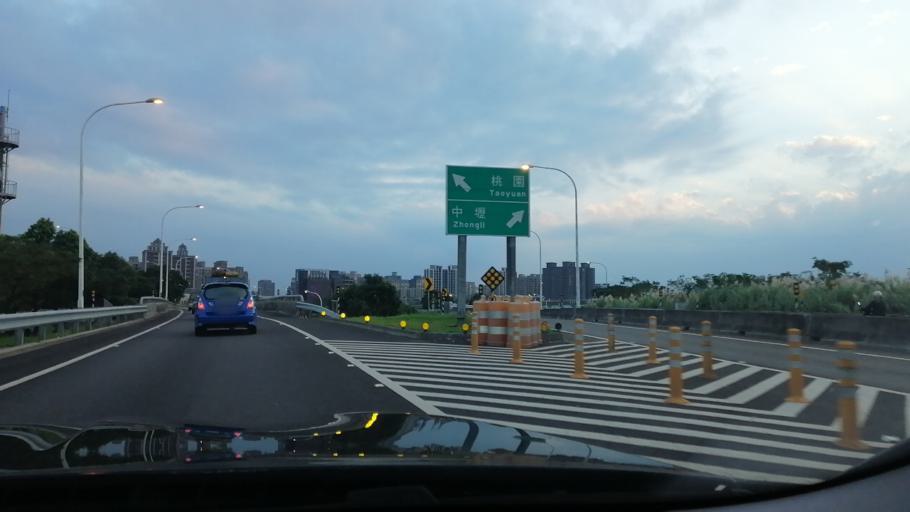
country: TW
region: Taiwan
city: Taoyuan City
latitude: 24.9995
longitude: 121.2830
